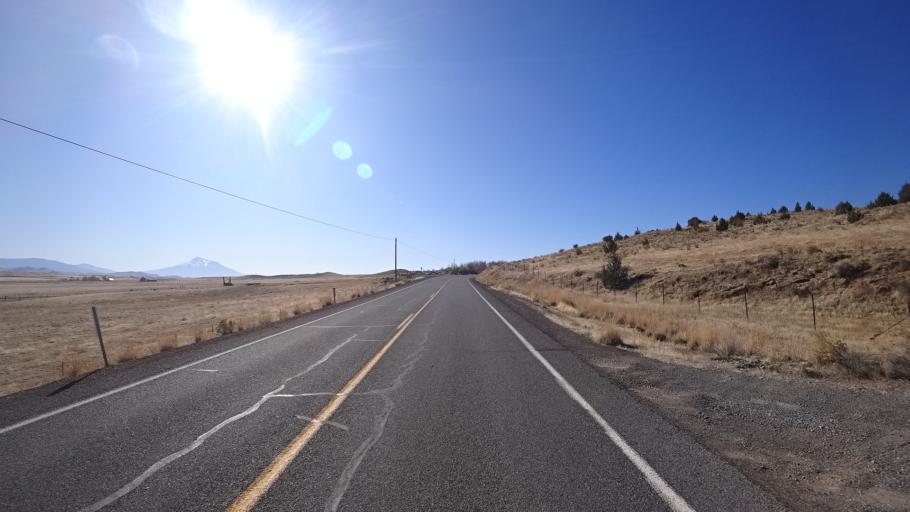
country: US
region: California
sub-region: Siskiyou County
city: Montague
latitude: 41.8223
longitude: -122.4945
